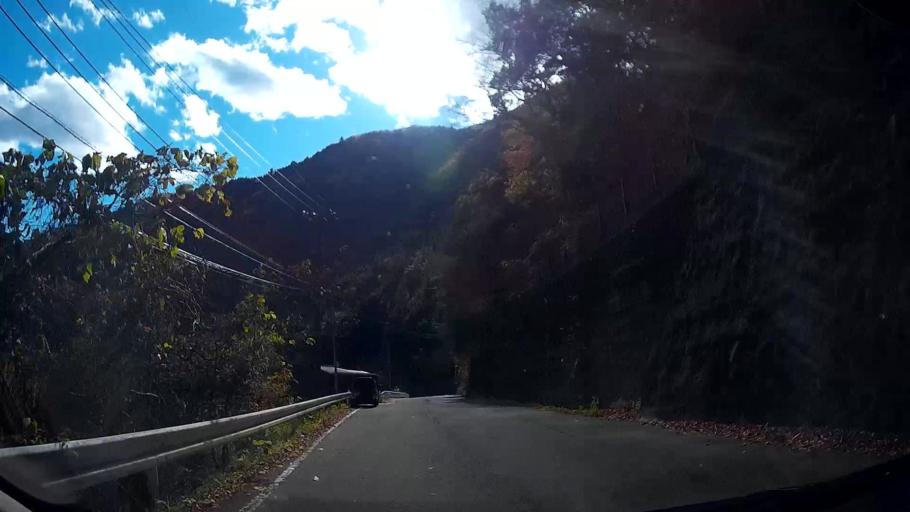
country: JP
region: Yamanashi
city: Otsuki
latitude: 35.6883
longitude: 138.9646
